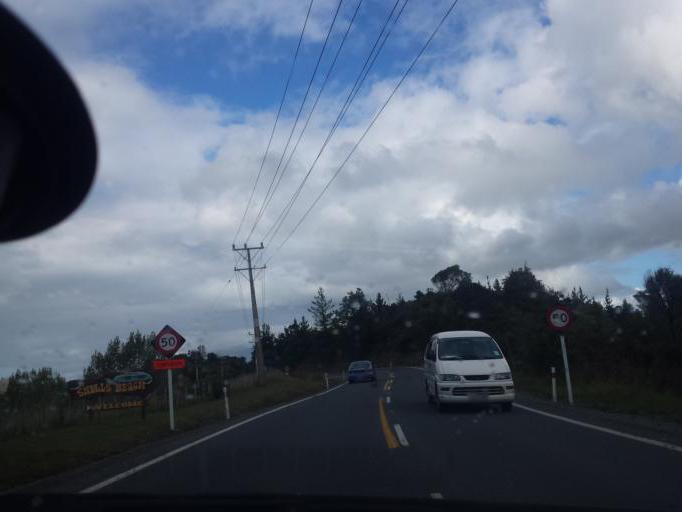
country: NZ
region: Auckland
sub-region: Auckland
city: Warkworth
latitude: -36.4058
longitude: 174.7184
